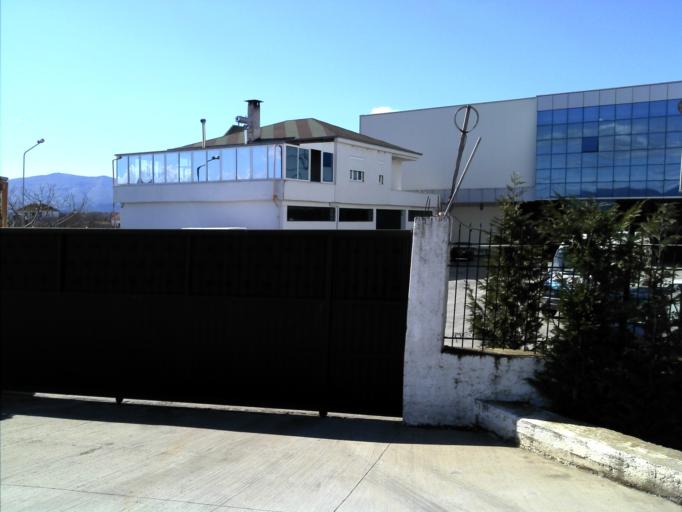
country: AL
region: Shkoder
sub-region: Rrethi i Shkodres
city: Shkoder
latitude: 42.1134
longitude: 19.4990
